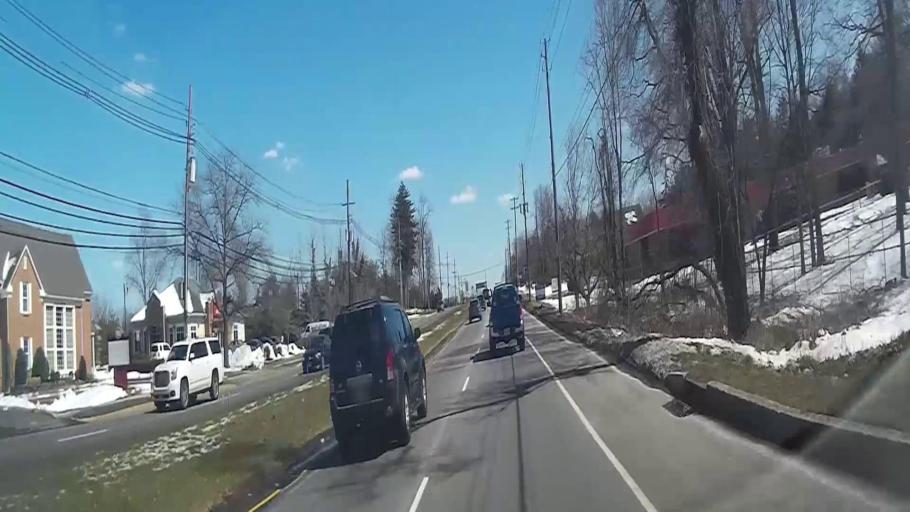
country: US
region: New Jersey
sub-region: Camden County
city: Springdale
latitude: 39.9008
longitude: -74.9613
